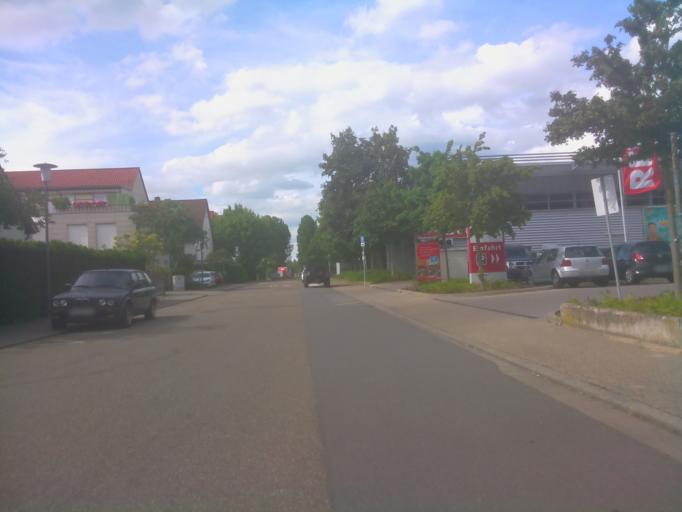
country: DE
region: Baden-Wuerttemberg
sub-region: Karlsruhe Region
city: Dossenheim
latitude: 49.4358
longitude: 8.6781
